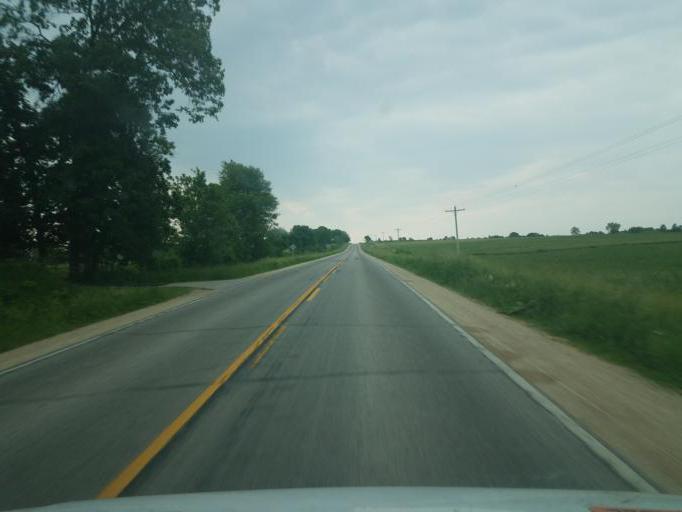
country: US
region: Wisconsin
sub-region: Vernon County
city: Hillsboro
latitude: 43.6303
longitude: -90.4526
